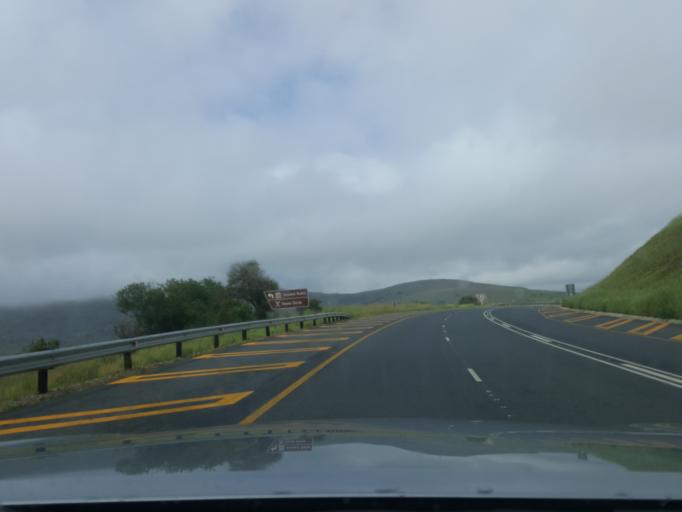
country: ZA
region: Mpumalanga
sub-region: Nkangala District Municipality
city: Belfast
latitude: -25.6291
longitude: 30.3264
